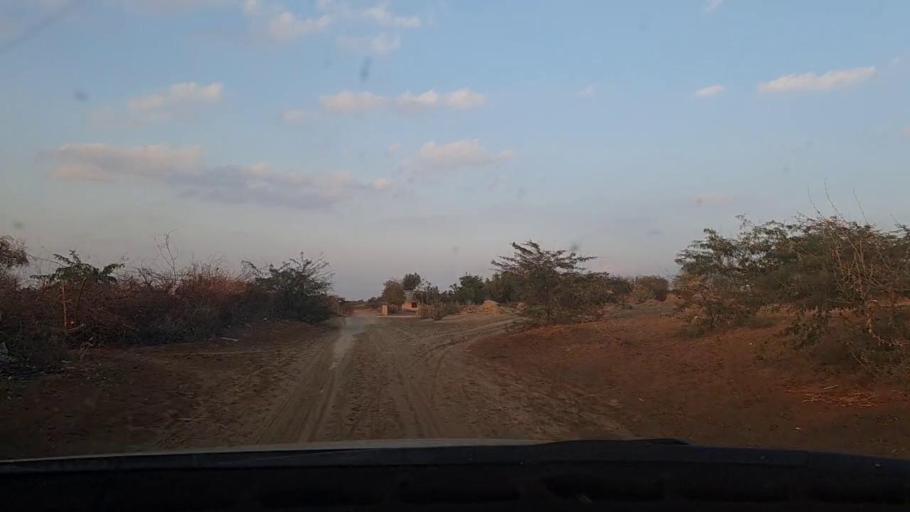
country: PK
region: Sindh
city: Tando Mittha Khan
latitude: 25.9397
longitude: 69.3378
